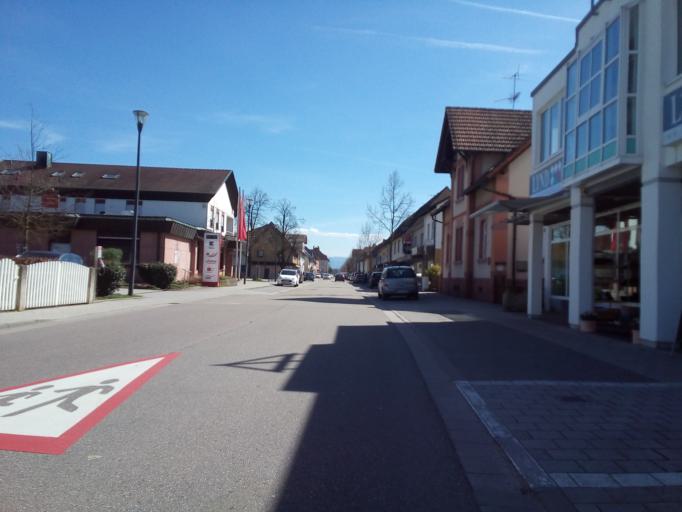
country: DE
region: Baden-Wuerttemberg
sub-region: Freiburg Region
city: Rheinau
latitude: 48.6657
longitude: 7.9367
